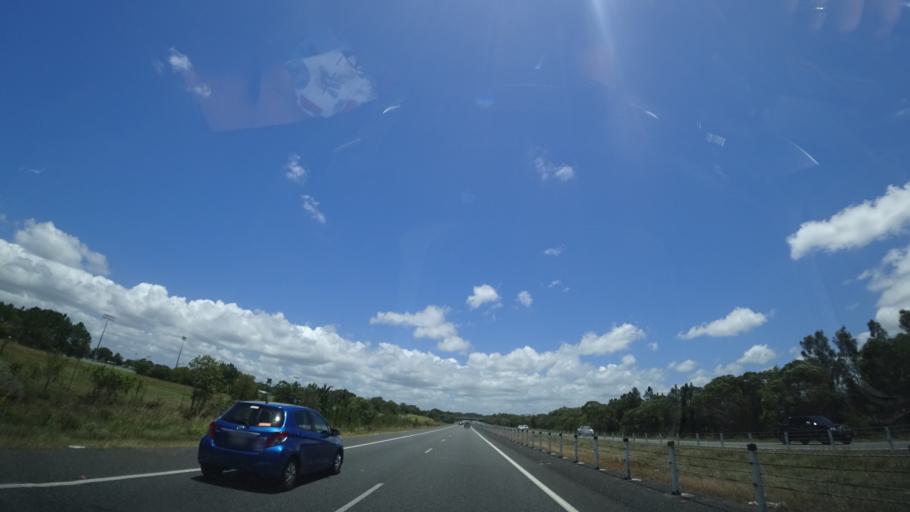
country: AU
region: Queensland
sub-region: Sunshine Coast
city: Little Mountain
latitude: -26.7810
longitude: 153.0751
